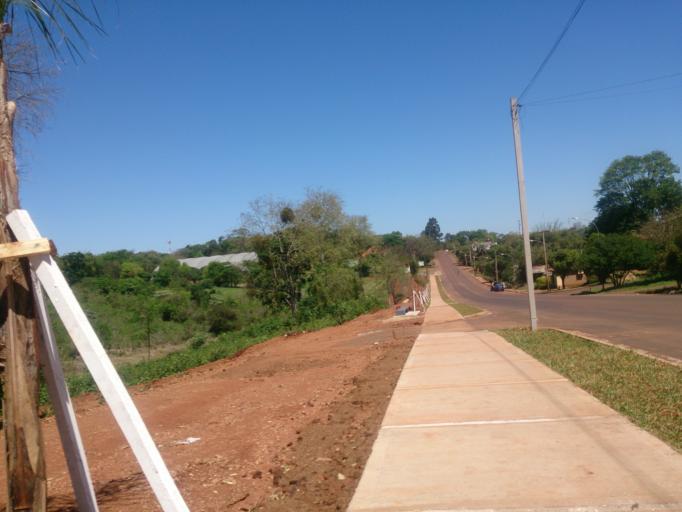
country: AR
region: Misiones
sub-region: Departamento de Obera
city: Obera
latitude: -27.4951
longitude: -55.1122
